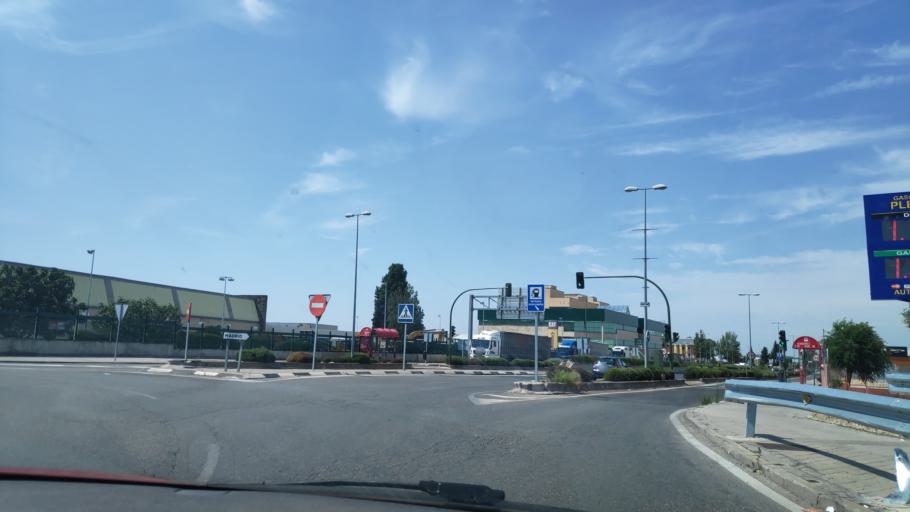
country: ES
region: Madrid
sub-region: Provincia de Madrid
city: Arganda
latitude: 40.3064
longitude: -3.4635
